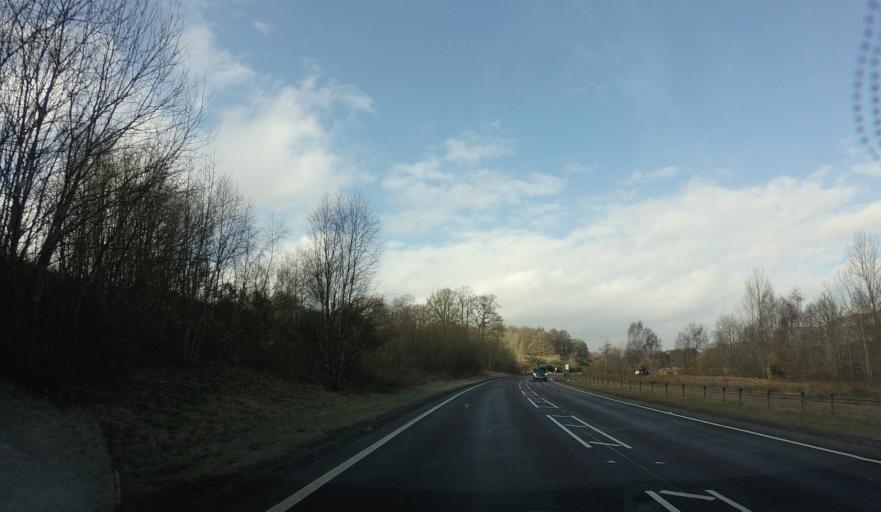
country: GB
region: Scotland
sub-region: Perth and Kinross
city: Pitlochry
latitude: 56.6918
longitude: -3.7247
